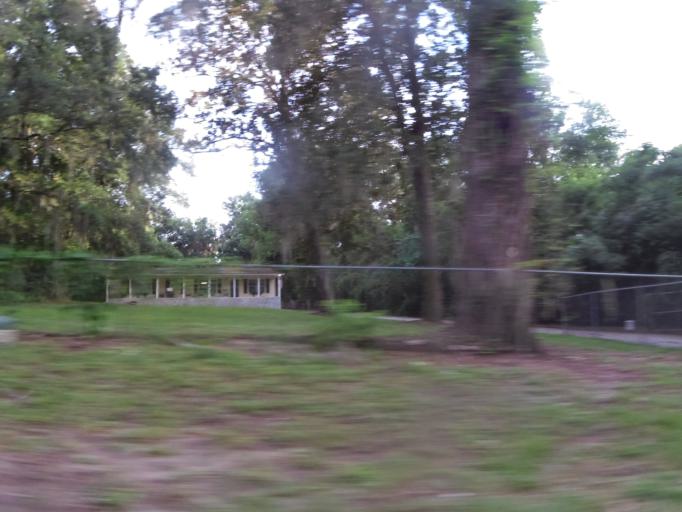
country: US
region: Florida
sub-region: Duval County
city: Jacksonville
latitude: 30.4165
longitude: -81.7123
